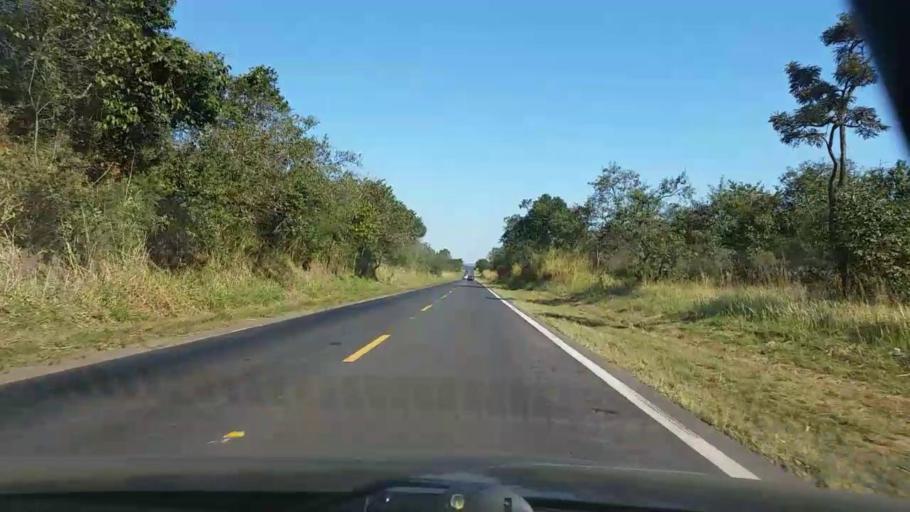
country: BR
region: Sao Paulo
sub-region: Itatinga
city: Itatinga
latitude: -22.8959
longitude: -48.7638
